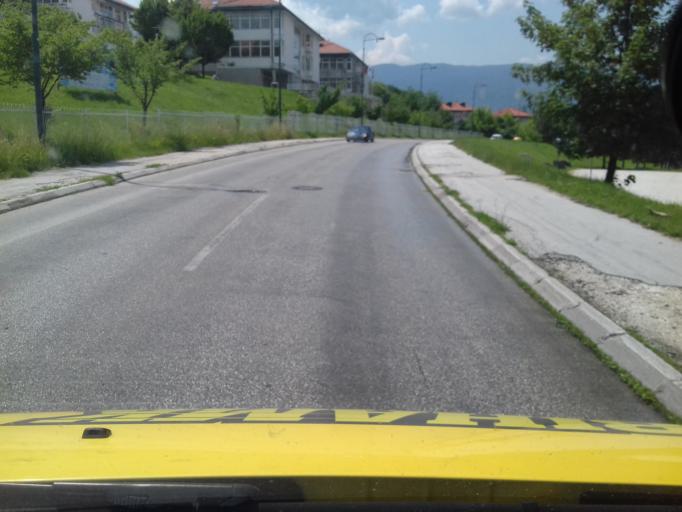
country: BA
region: Federation of Bosnia and Herzegovina
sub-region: Kanton Sarajevo
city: Sarajevo
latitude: 43.8379
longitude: 18.3487
